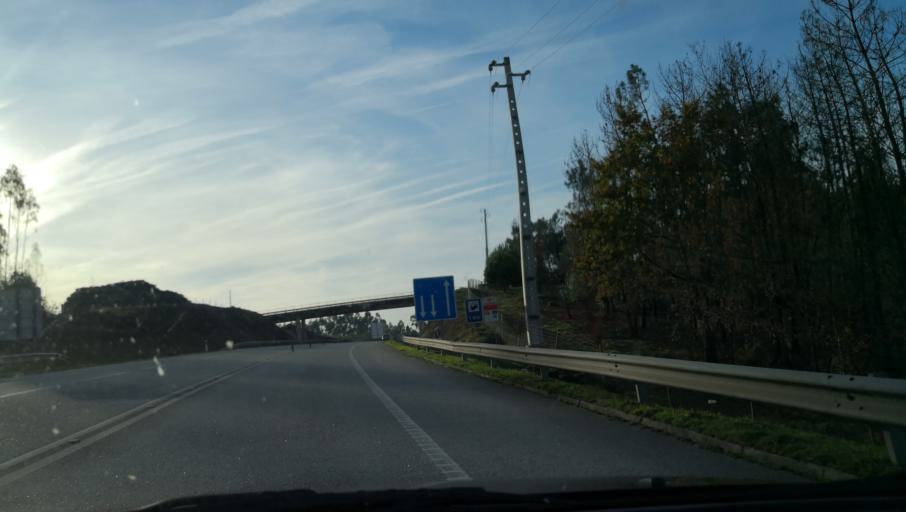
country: PT
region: Viseu
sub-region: Santa Comba Dao
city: Santa Comba Dao
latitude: 40.3506
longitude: -8.1596
